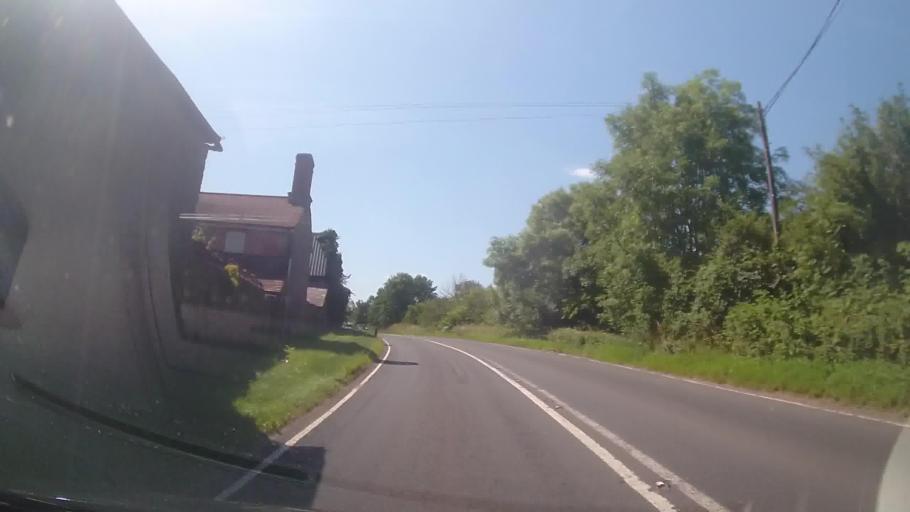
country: GB
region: England
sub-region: Herefordshire
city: Withington
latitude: 52.0801
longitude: -2.6263
